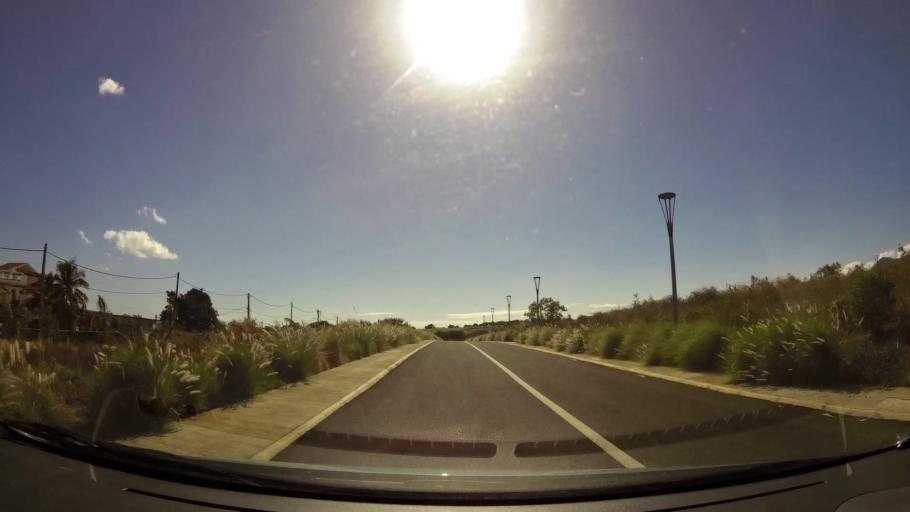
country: MU
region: Black River
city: Flic en Flac
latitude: -20.2651
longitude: 57.3789
